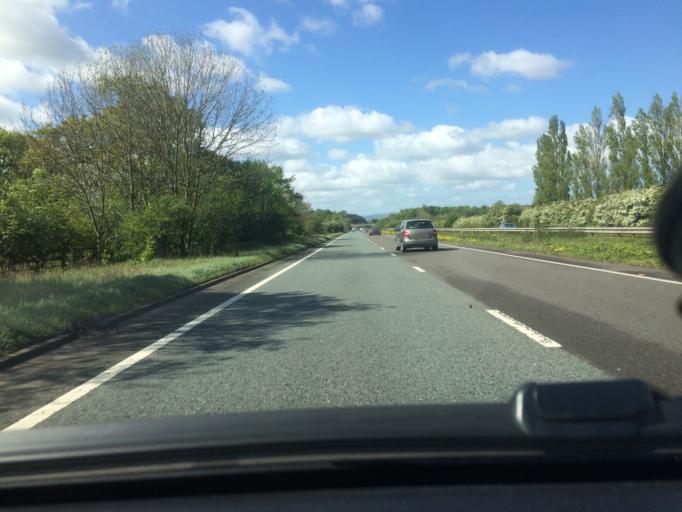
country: GB
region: England
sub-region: Cheshire West and Chester
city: Eccleston
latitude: 53.1654
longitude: -2.8711
